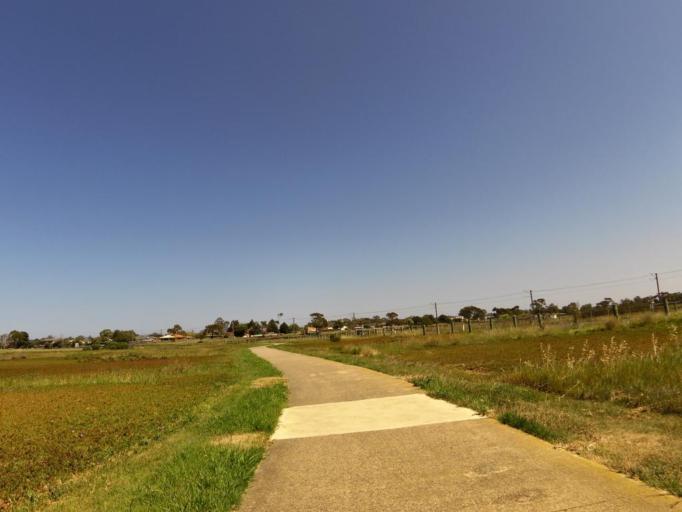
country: AU
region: Victoria
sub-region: Hobsons Bay
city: Seaholme
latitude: -37.8576
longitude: 144.8516
